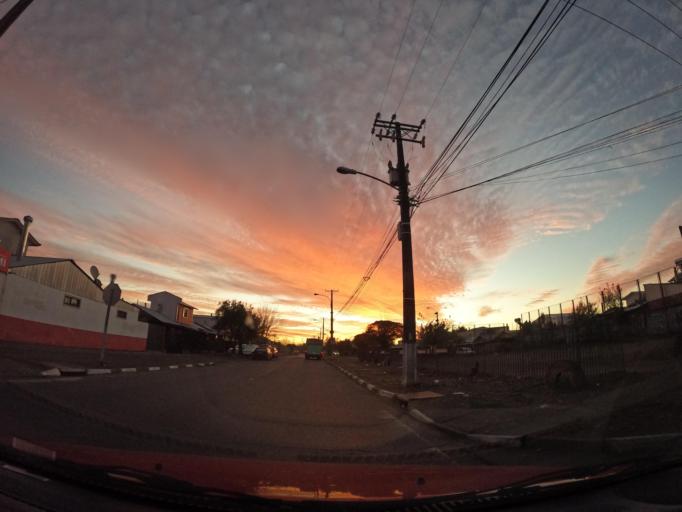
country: CL
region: Biobio
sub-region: Provincia de Nuble
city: Chillan
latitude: -36.6299
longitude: -72.1010
